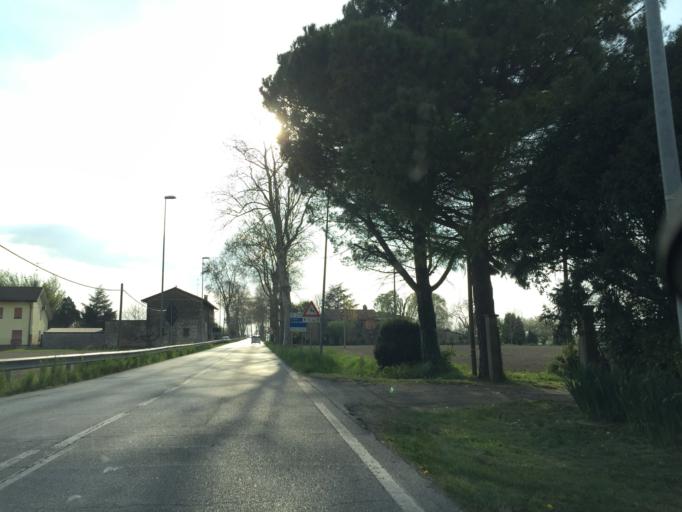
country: IT
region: Veneto
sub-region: Provincia di Venezia
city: San Michele al Tagliamento
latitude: 45.7479
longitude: 12.9886
